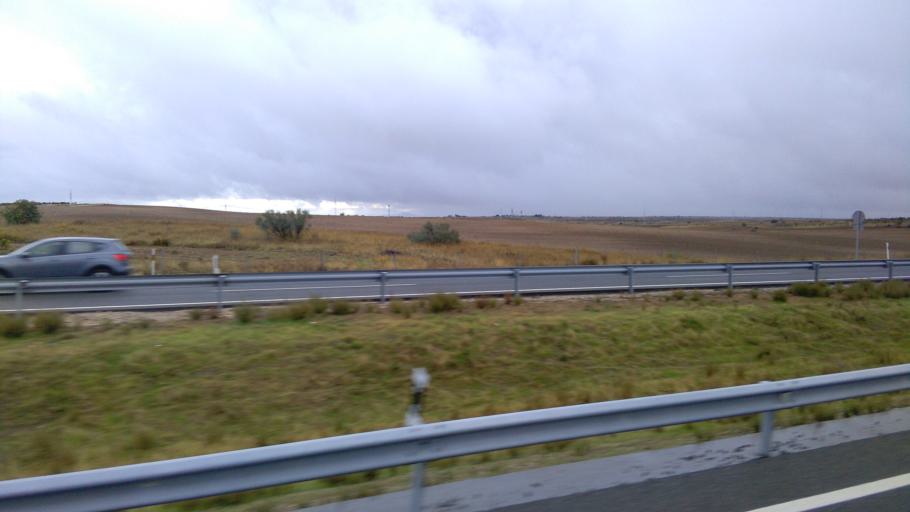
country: ES
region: Castille-La Mancha
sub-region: Province of Toledo
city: Las Ventas de Retamosa
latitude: 40.1865
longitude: -4.1292
